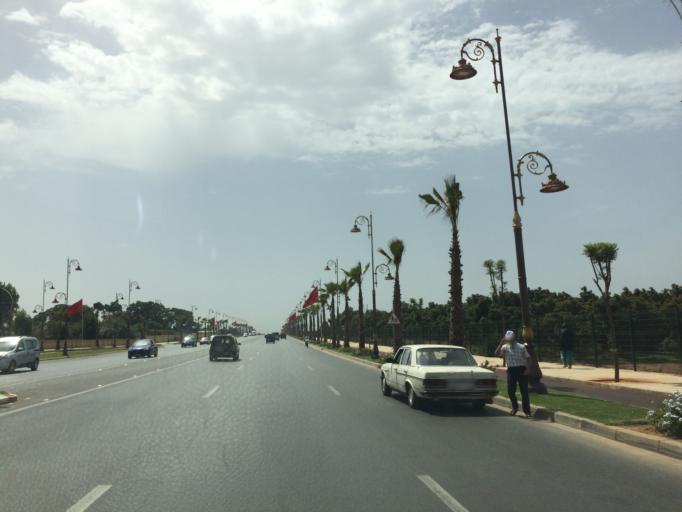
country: MA
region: Rabat-Sale-Zemmour-Zaer
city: Sale
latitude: 34.0314
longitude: -6.7579
